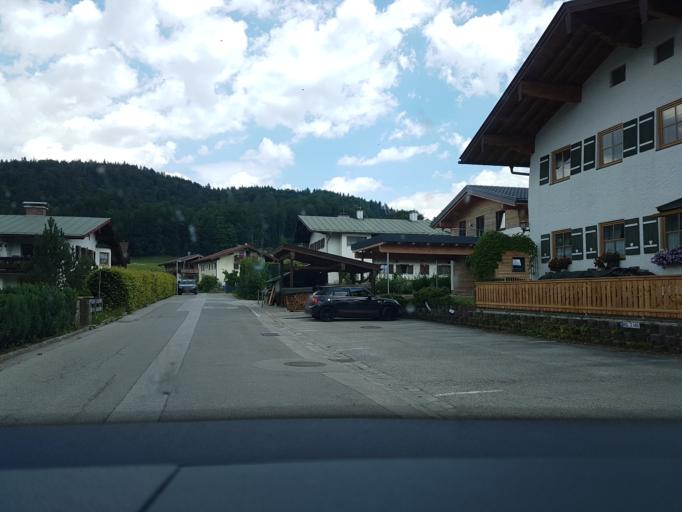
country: DE
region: Bavaria
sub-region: Upper Bavaria
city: Berchtesgaden
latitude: 47.6331
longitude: 12.9771
